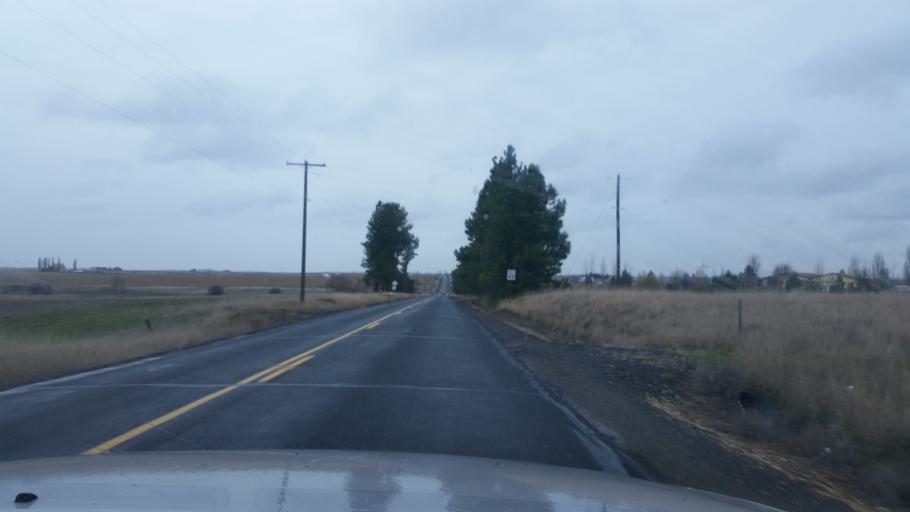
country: US
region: Washington
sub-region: Spokane County
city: Medical Lake
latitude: 47.6164
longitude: -117.7334
